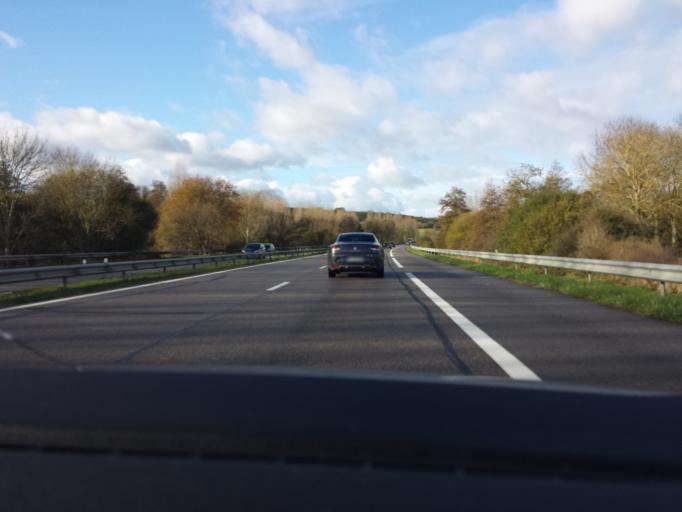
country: FR
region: Haute-Normandie
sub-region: Departement de l'Eure
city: Pacy-sur-Eure
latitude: 49.0077
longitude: 1.3722
